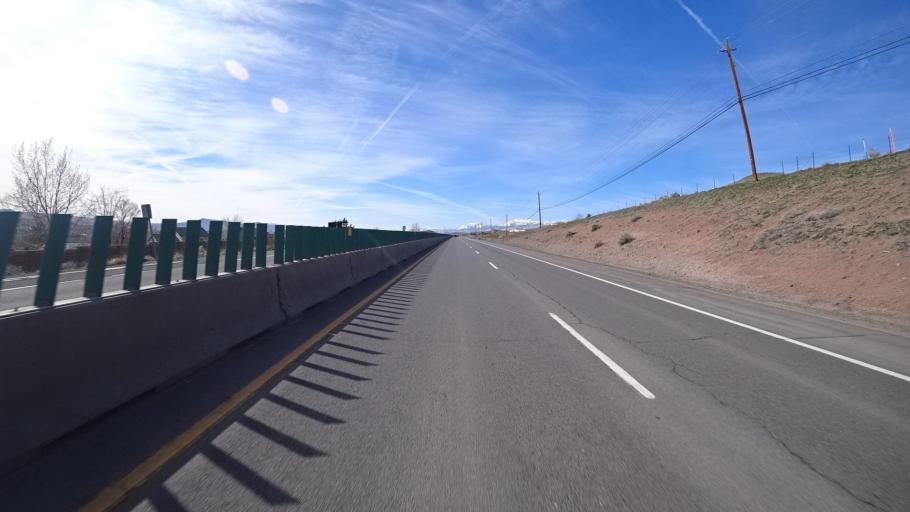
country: US
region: Nevada
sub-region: Washoe County
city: Sun Valley
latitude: 39.6020
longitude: -119.7352
